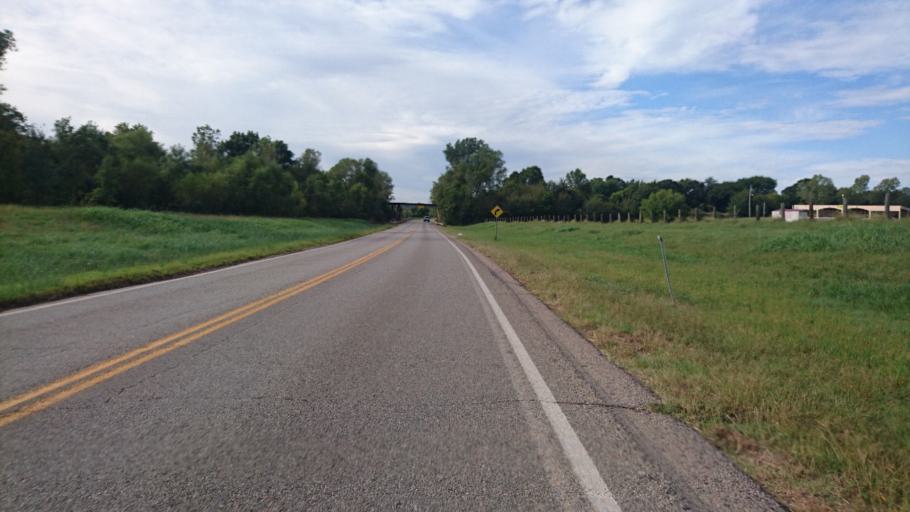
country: US
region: Oklahoma
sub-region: Lincoln County
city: Chandler
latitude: 35.6852
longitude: -97.0009
